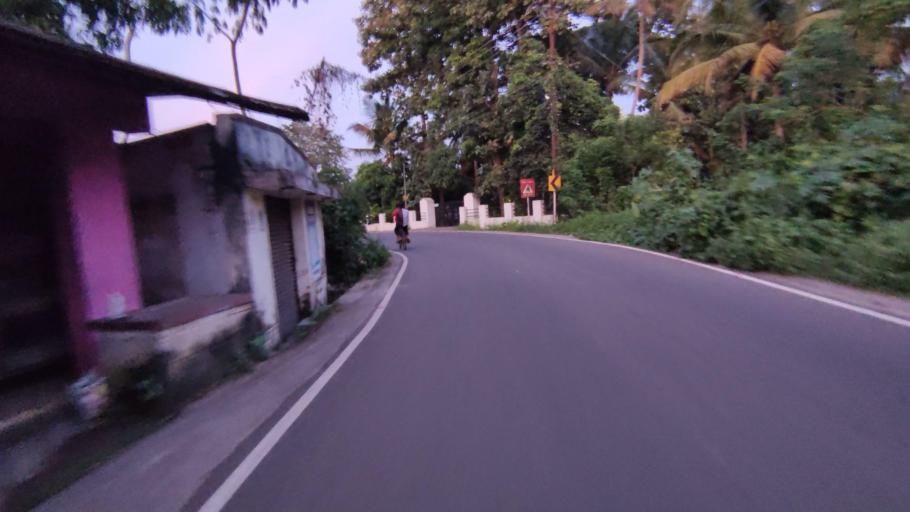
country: IN
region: Kerala
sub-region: Kottayam
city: Kottayam
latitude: 9.5863
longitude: 76.4371
